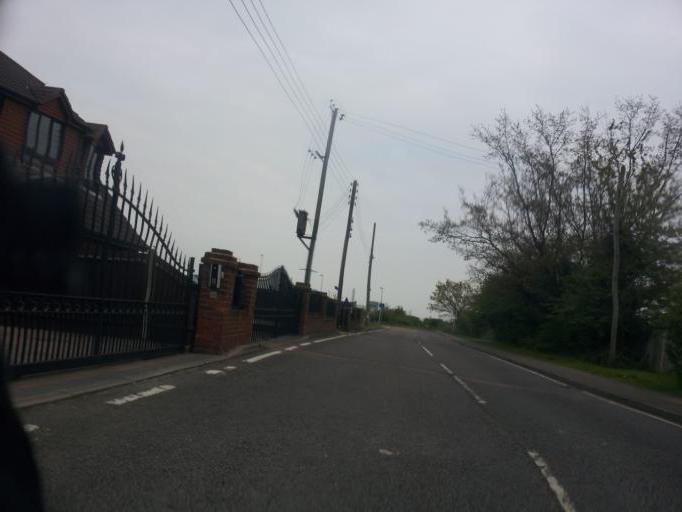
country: GB
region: England
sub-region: Kent
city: Hoo
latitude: 51.4195
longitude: 0.5364
